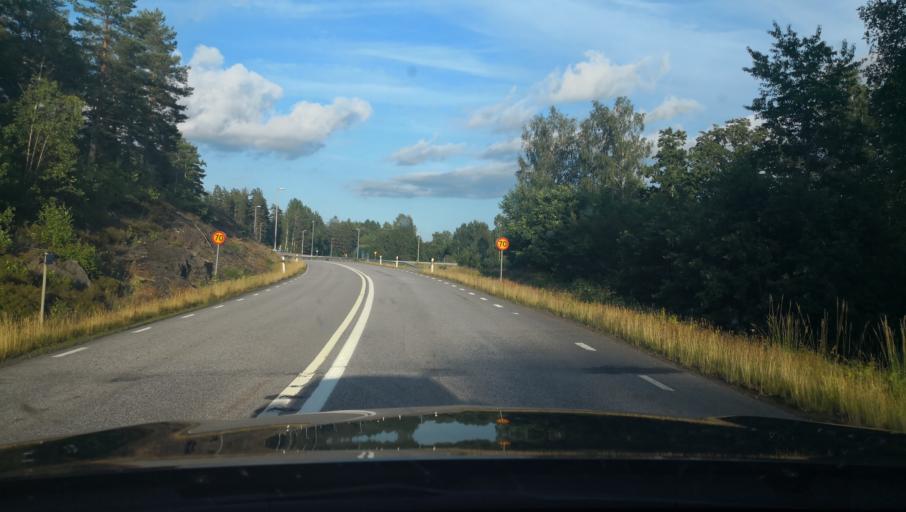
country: SE
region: Kalmar
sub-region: Hultsfreds Kommun
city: Malilla
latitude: 57.3894
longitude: 15.7530
